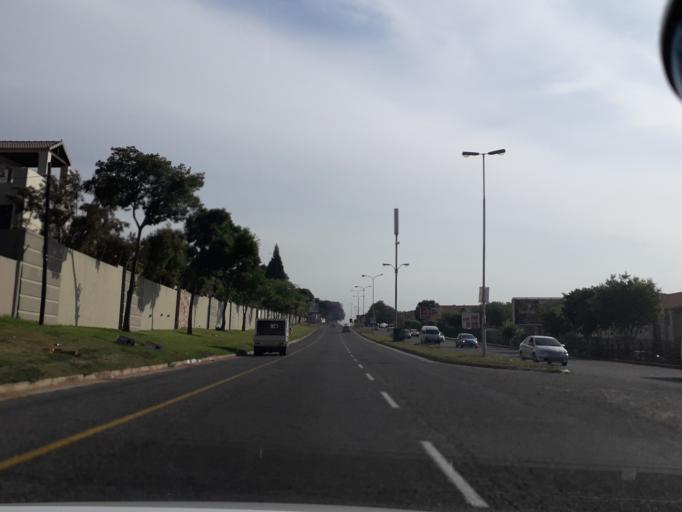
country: ZA
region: Gauteng
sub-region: City of Johannesburg Metropolitan Municipality
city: Diepsloot
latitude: -26.0660
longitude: 28.0195
